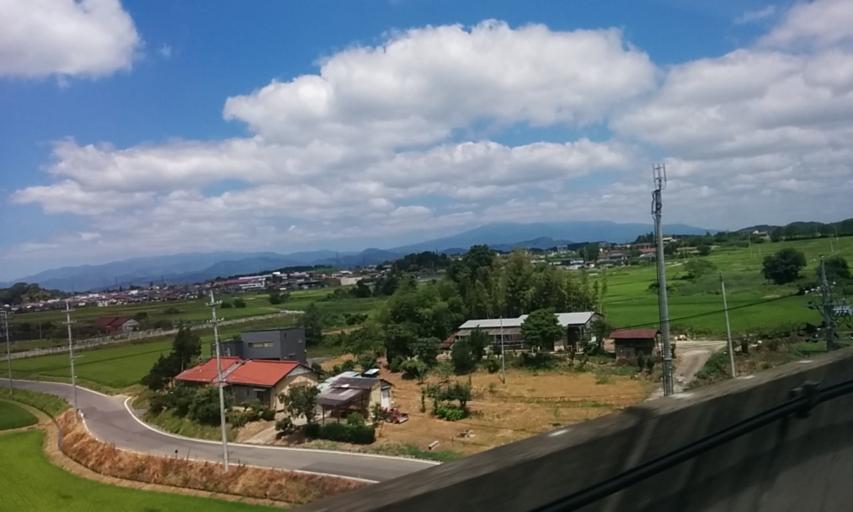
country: JP
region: Fukushima
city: Koriyama
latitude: 37.4411
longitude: 140.4024
